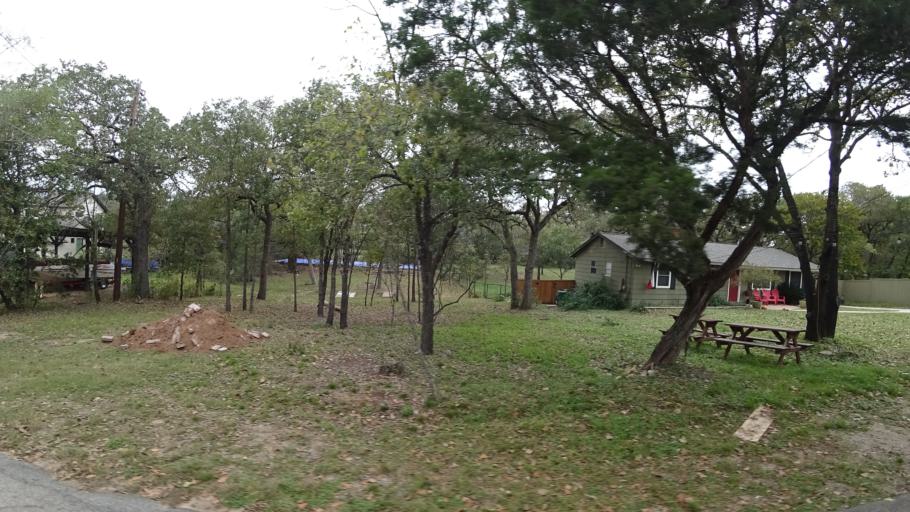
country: US
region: Texas
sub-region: Travis County
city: Bee Cave
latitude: 30.3323
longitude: -97.9259
